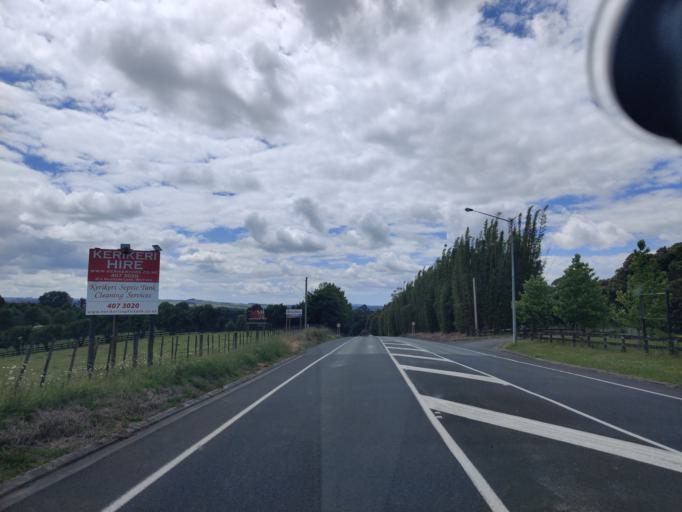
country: NZ
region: Northland
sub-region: Far North District
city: Kerikeri
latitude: -35.2531
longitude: 173.9314
